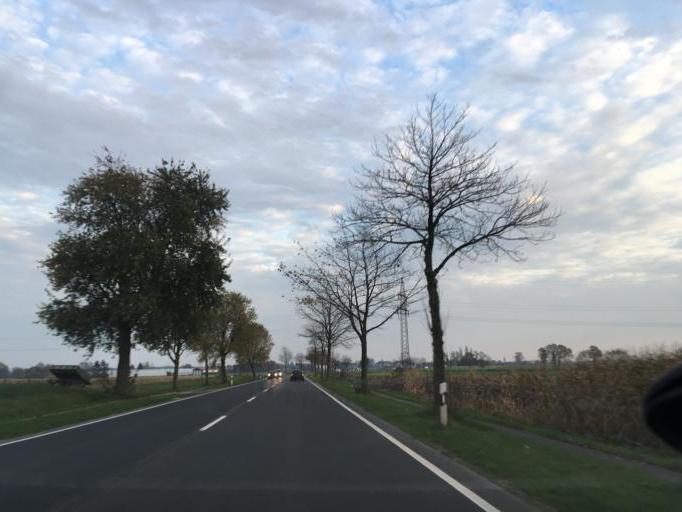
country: DE
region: Lower Saxony
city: Celle
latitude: 52.6504
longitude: 10.0688
